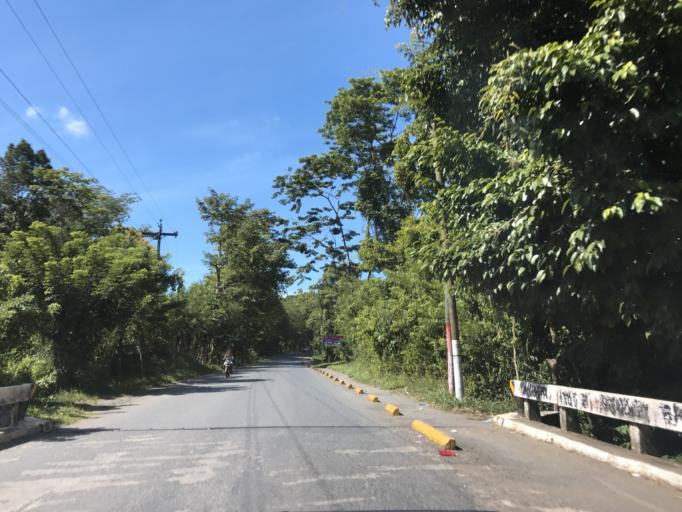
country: GT
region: Izabal
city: Morales
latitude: 15.6547
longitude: -89.0086
